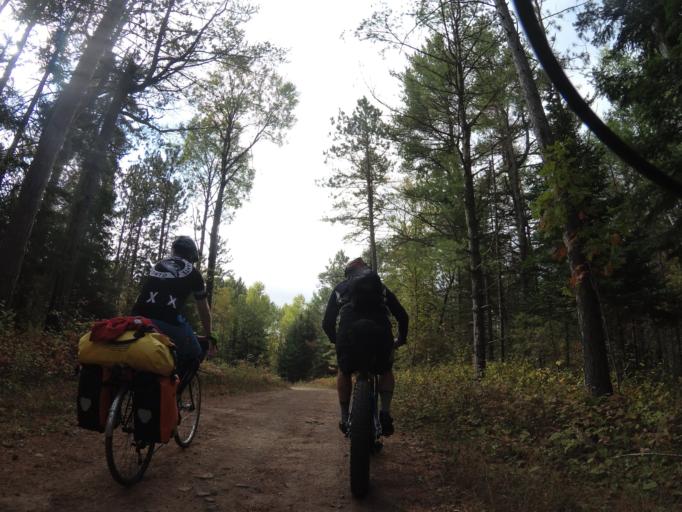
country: CA
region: Ontario
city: Pembroke
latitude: 45.2681
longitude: -77.2126
